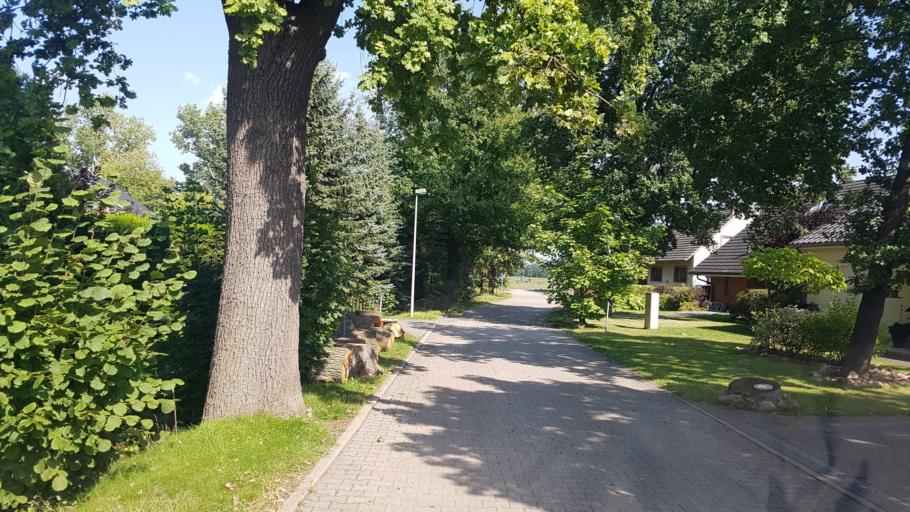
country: DE
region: Brandenburg
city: Calau
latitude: 51.7460
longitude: 13.9795
